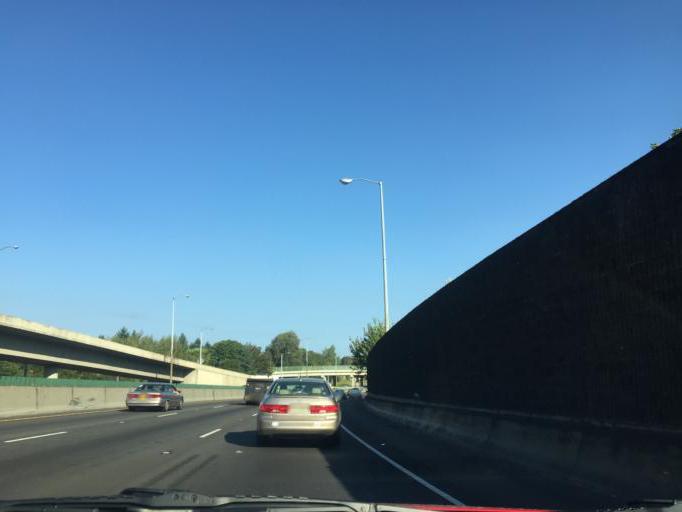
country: US
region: Oregon
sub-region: Multnomah County
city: Portland
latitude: 45.5318
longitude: -122.6184
